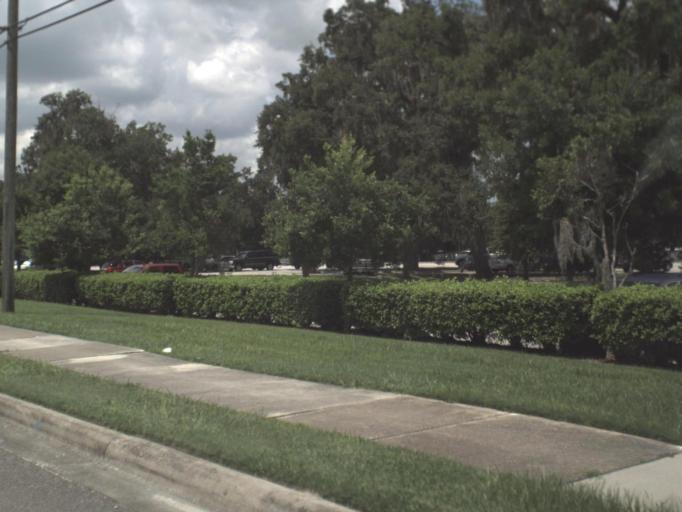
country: US
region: Florida
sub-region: Hernando County
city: South Brooksville
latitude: 28.5361
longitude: -82.4063
